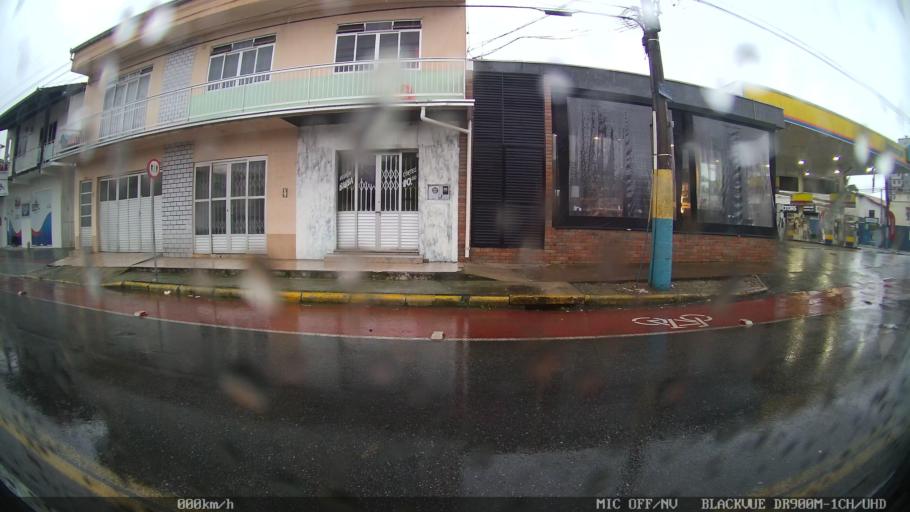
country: BR
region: Santa Catarina
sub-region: Navegantes
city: Navegantes
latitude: -26.8964
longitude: -48.6476
